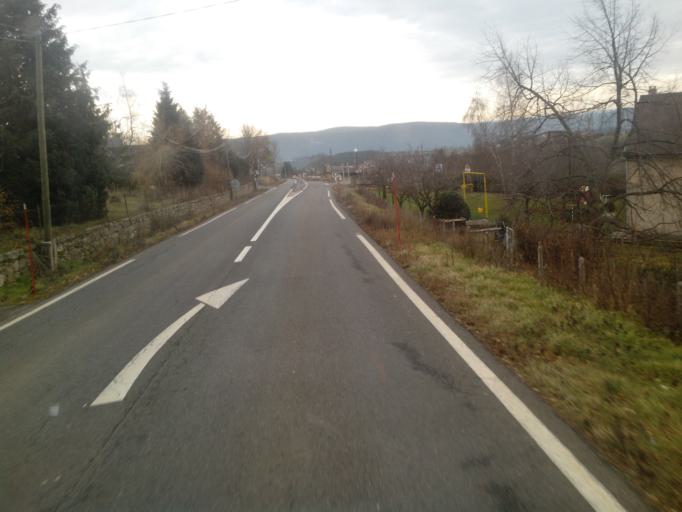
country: FR
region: Languedoc-Roussillon
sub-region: Departement de la Lozere
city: Mende
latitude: 44.5592
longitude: 3.5043
